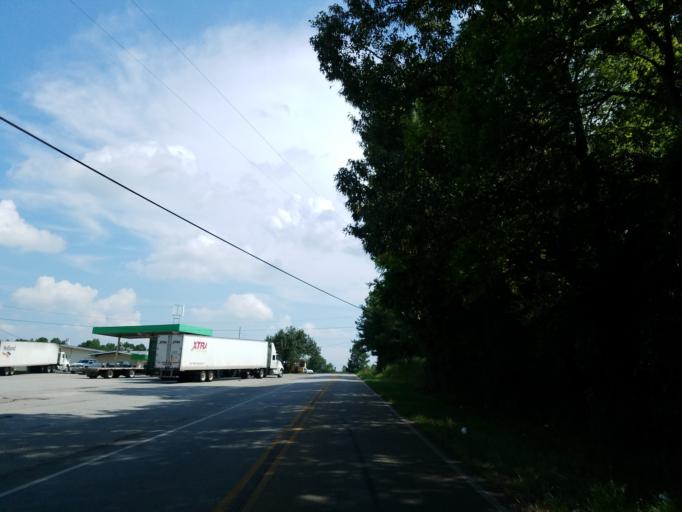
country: US
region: Georgia
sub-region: Monroe County
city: Forsyth
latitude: 32.9935
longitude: -83.8432
